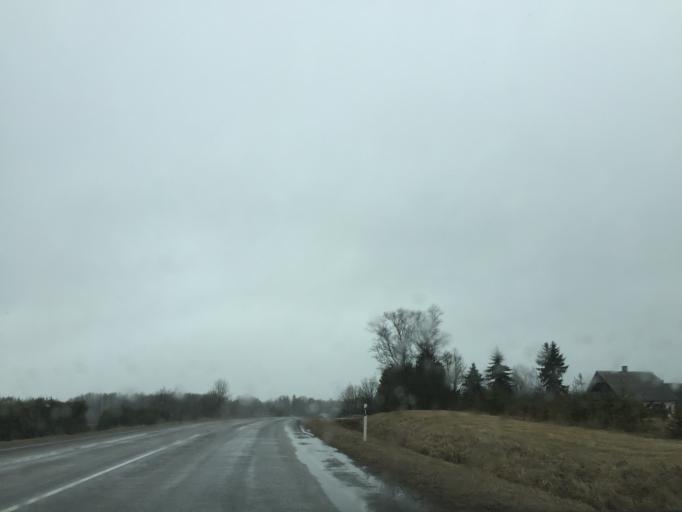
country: EE
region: Laeaene
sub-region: Ridala Parish
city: Uuemoisa
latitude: 58.8820
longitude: 23.6026
